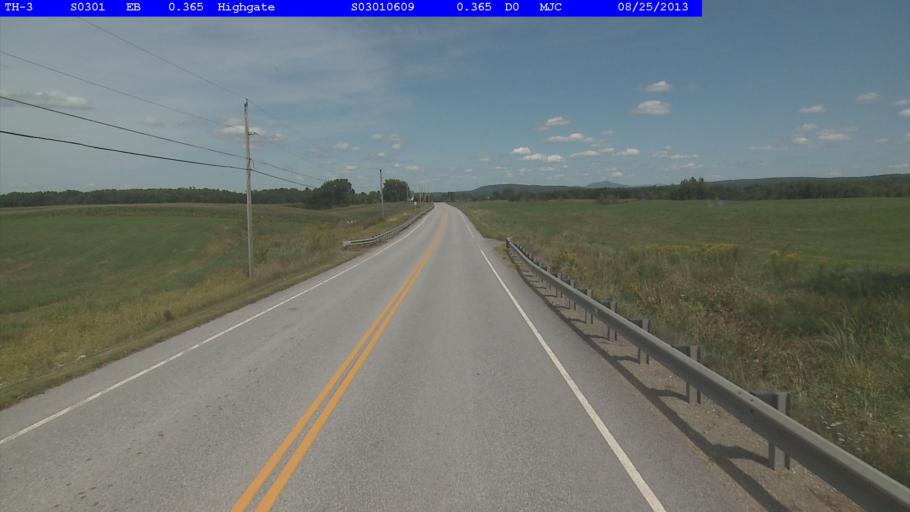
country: US
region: Vermont
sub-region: Franklin County
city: Swanton
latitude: 44.9501
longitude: -73.0096
